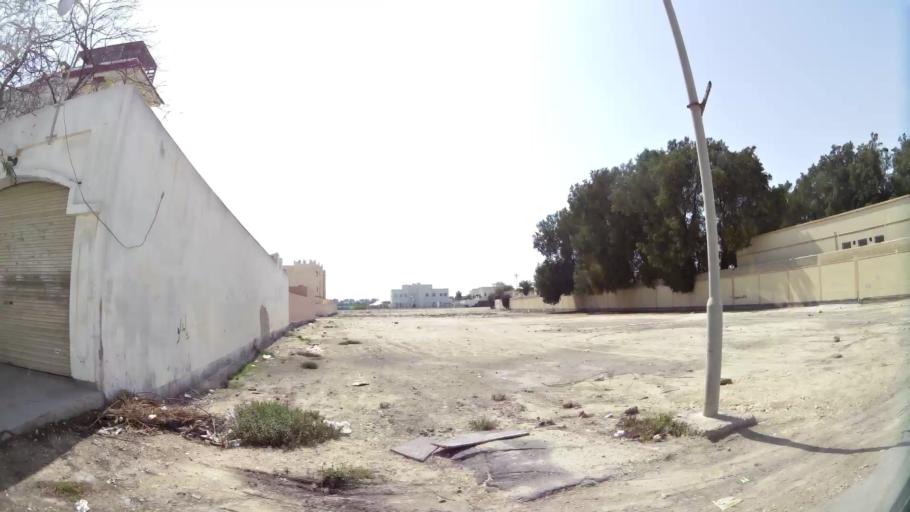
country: BH
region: Northern
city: Madinat `Isa
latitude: 26.1948
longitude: 50.4652
